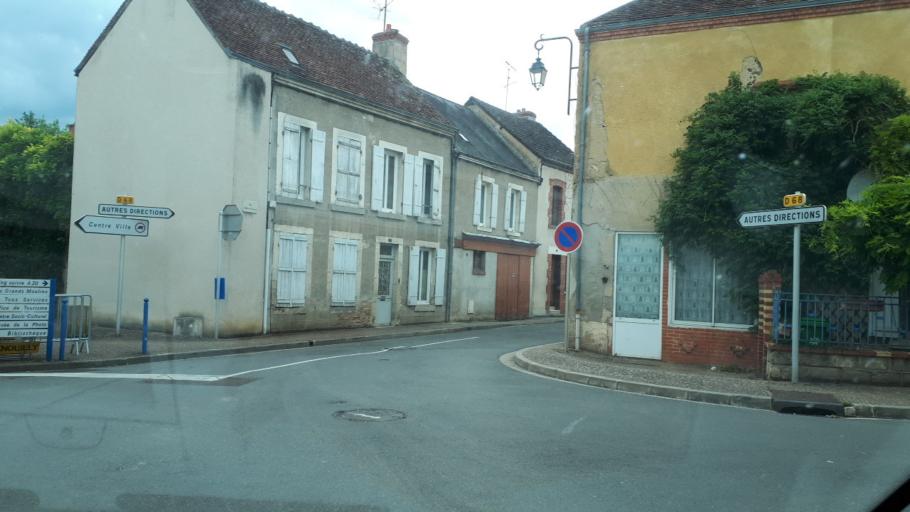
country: FR
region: Centre
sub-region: Departement du Cher
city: Gracay
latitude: 47.1443
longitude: 1.8471
